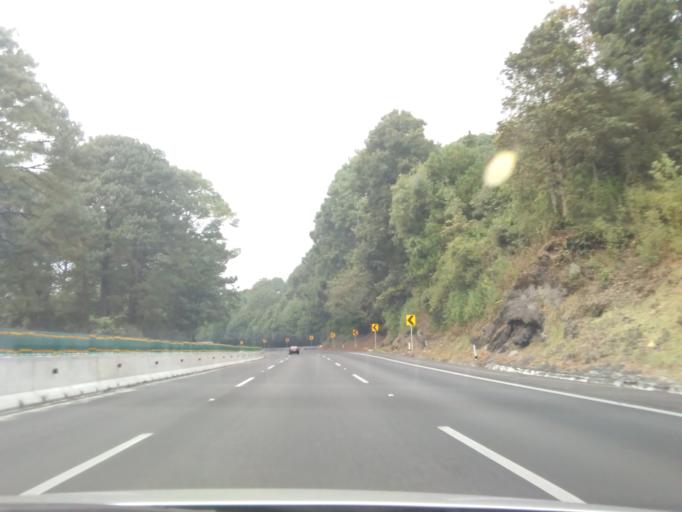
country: MX
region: Morelos
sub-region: Cuernavaca
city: Villa Santiago
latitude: 19.0279
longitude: -99.1792
